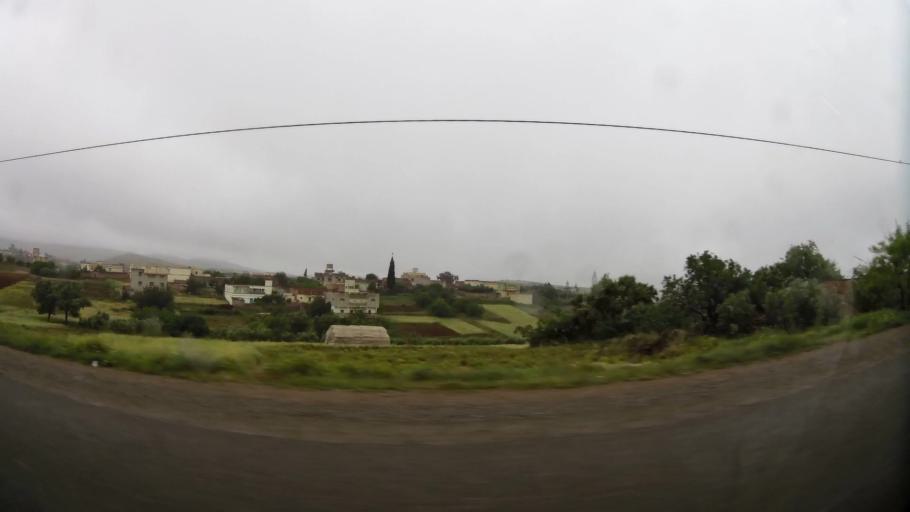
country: MA
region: Oriental
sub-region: Nador
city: Boudinar
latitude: 35.1225
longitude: -3.5753
